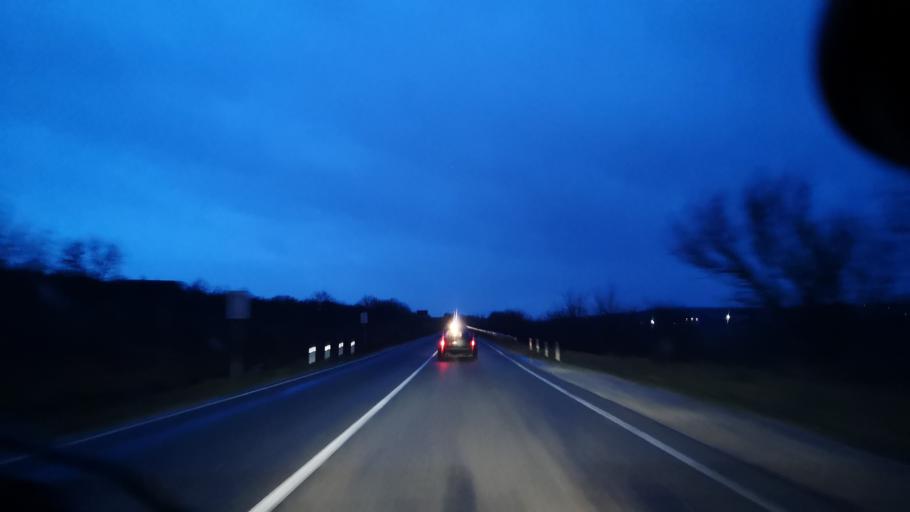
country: MD
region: Orhei
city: Orhei
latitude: 47.4061
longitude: 28.8166
